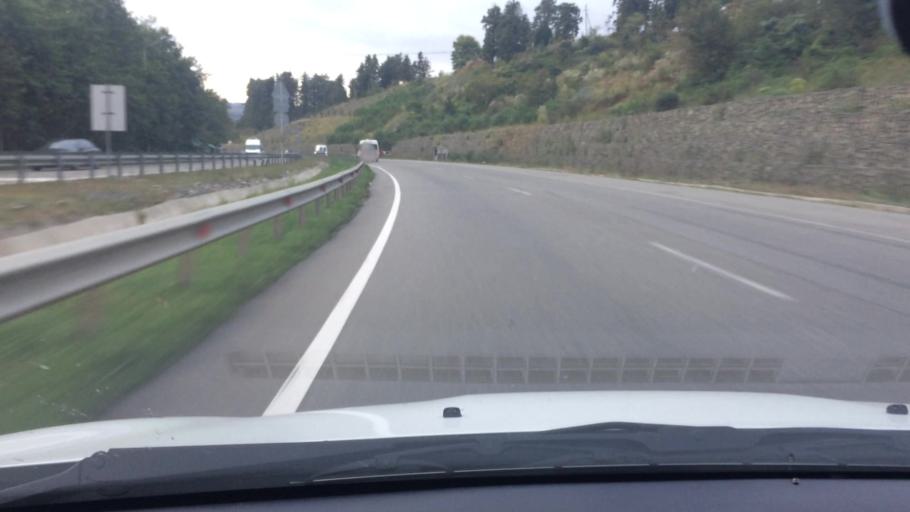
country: GE
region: Ajaria
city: Makhinjauri
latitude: 41.6944
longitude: 41.7257
